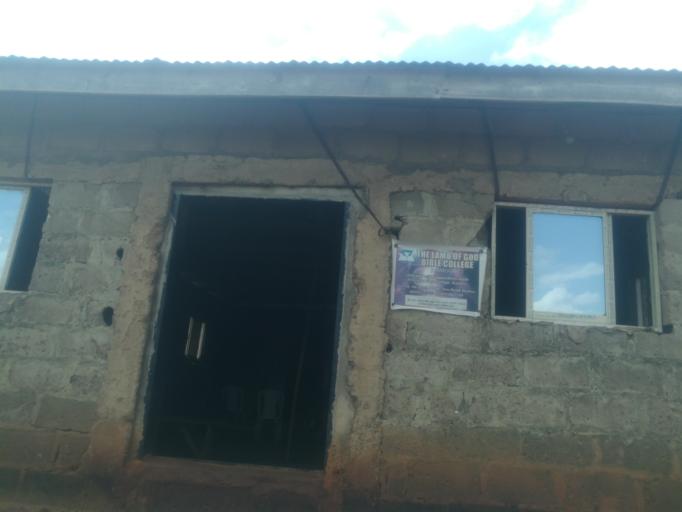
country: NG
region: Oyo
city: Egbeda
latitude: 7.4236
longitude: 3.9969
